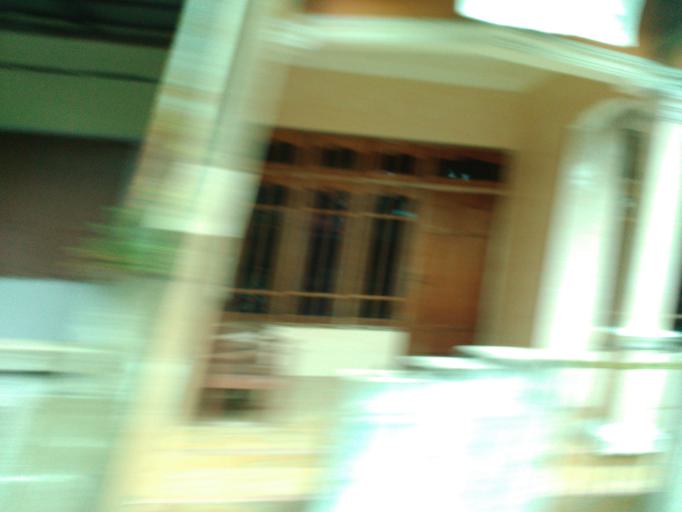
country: ID
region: Central Java
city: Delanggu
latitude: -7.6199
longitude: 110.7017
